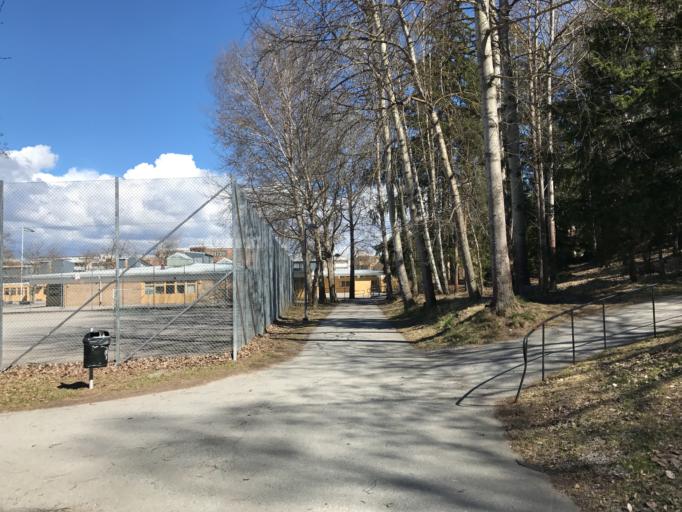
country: SE
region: Stockholm
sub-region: Stockholms Kommun
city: Kista
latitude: 59.4037
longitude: 17.9350
